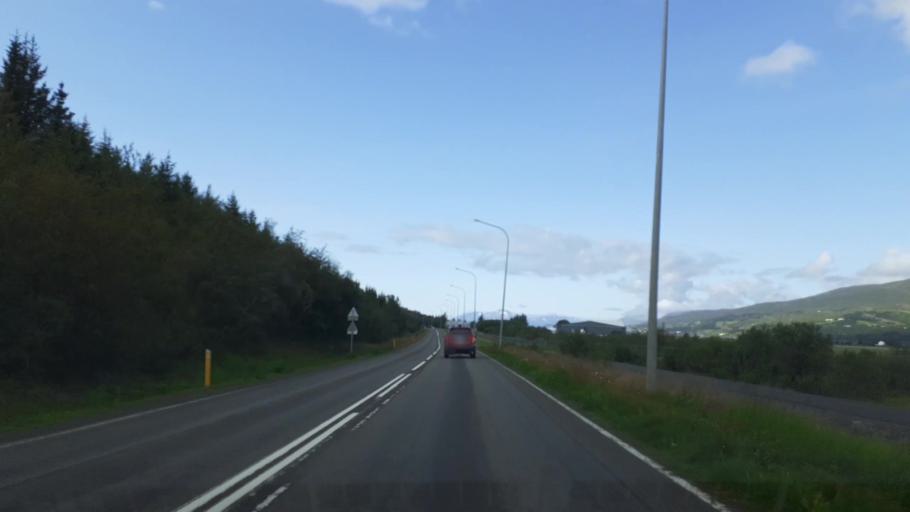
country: IS
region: Northeast
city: Akureyri
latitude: 65.6477
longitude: -18.0756
